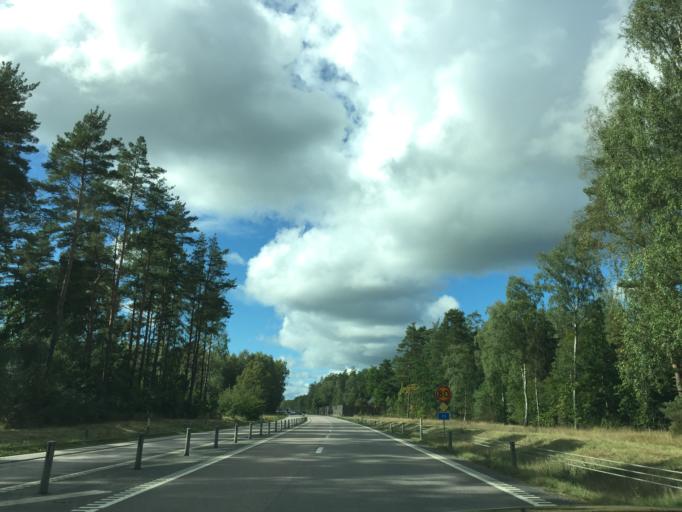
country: SE
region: Skane
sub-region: Sjobo Kommun
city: Sjoebo
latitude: 55.6362
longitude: 13.6679
